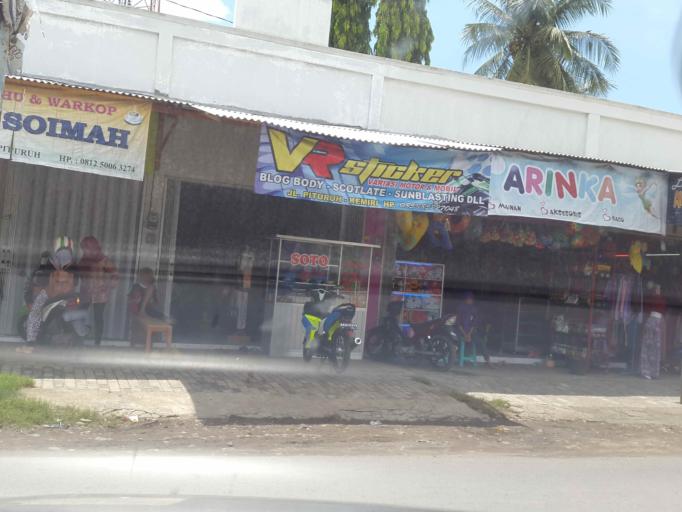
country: ID
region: Central Java
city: Kutoarjo
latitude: -7.6802
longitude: 109.8457
